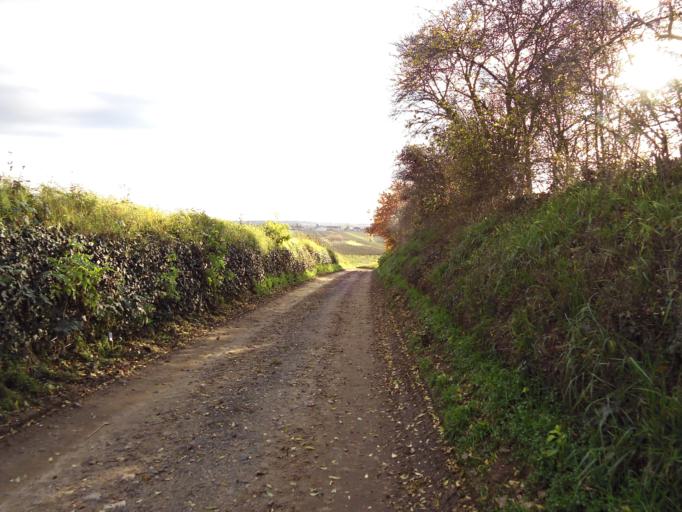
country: DE
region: Rheinland-Pfalz
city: Freinsheim
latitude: 49.4983
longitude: 8.2124
